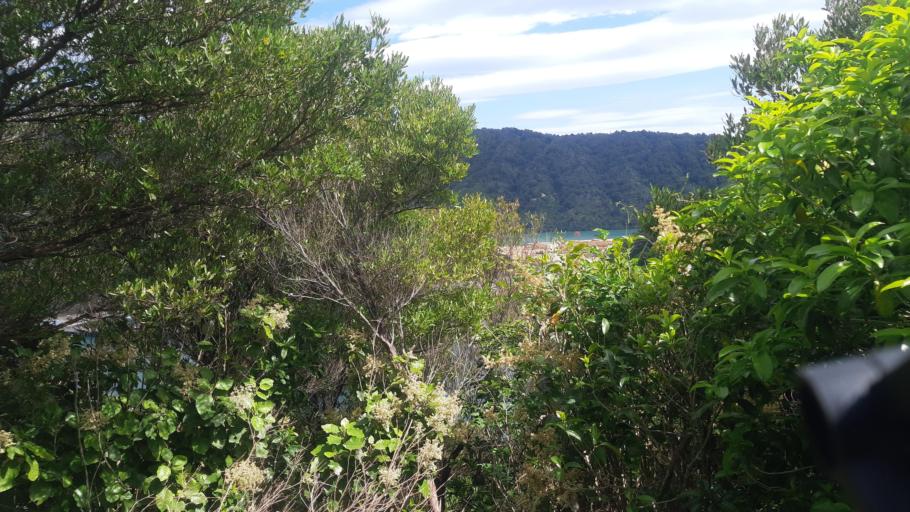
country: NZ
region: Marlborough
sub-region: Marlborough District
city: Picton
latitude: -41.2832
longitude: 174.0128
